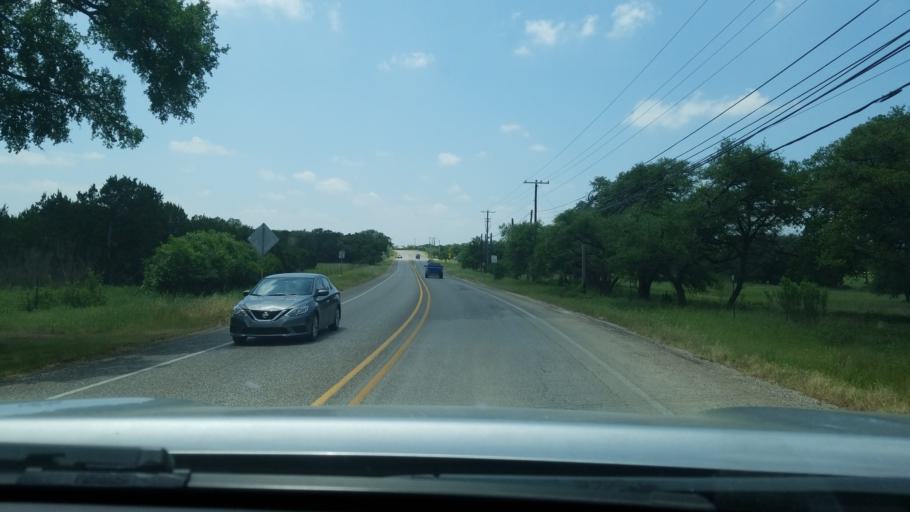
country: US
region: Texas
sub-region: Hays County
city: Woodcreek
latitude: 30.0205
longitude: -98.1352
